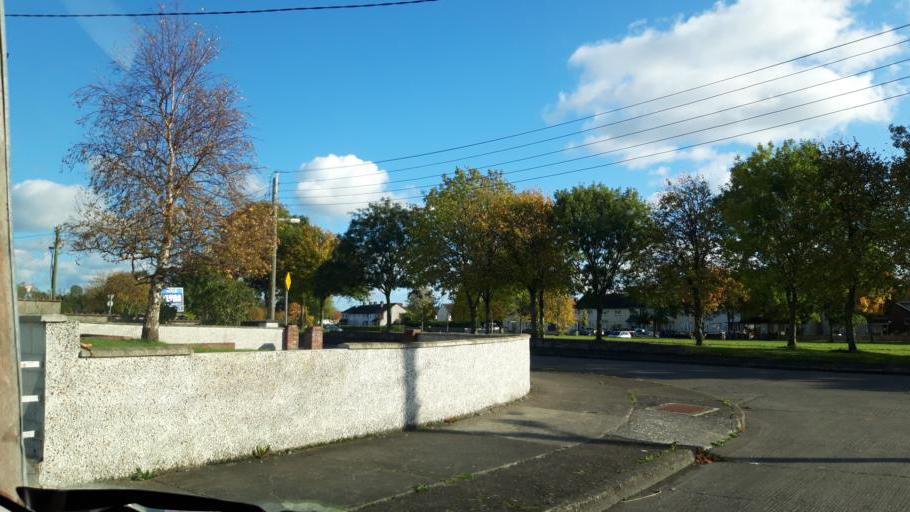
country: IE
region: Leinster
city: Raheny
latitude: 53.3847
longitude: -6.1839
